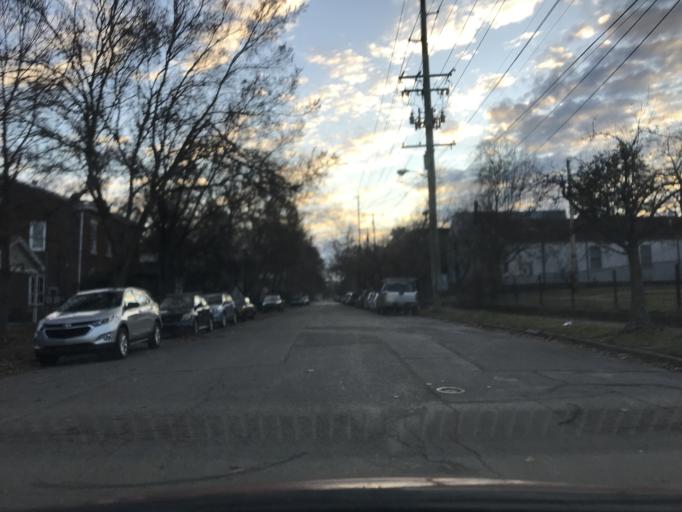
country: US
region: Indiana
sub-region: Clark County
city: Jeffersonville
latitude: 38.2563
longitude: -85.7374
